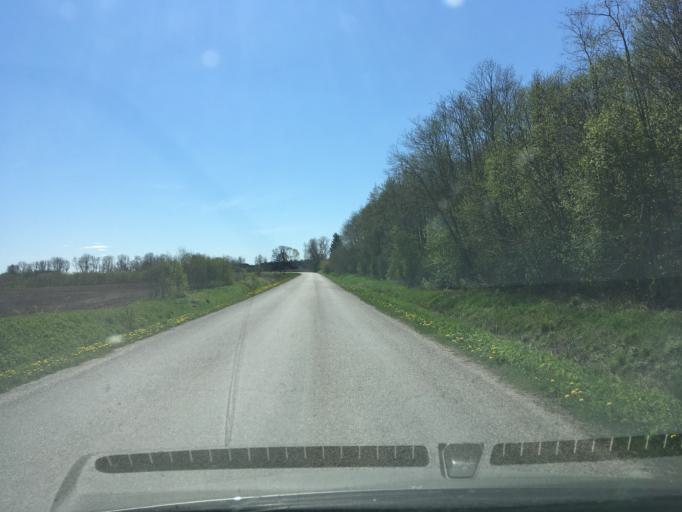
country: EE
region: Harju
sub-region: Raasiku vald
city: Arukula
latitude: 59.3959
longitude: 25.0795
